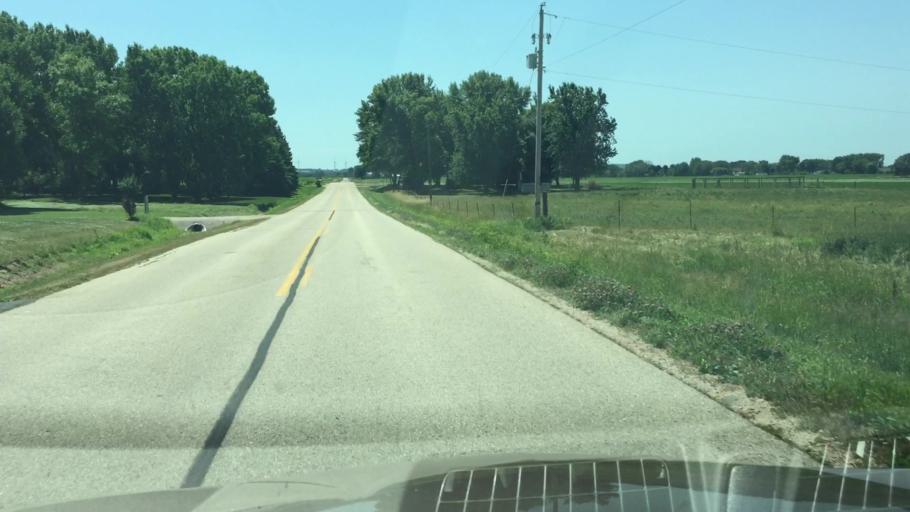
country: US
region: Wisconsin
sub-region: Fond du Lac County
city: Saint Peter
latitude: 43.9625
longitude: -88.3116
